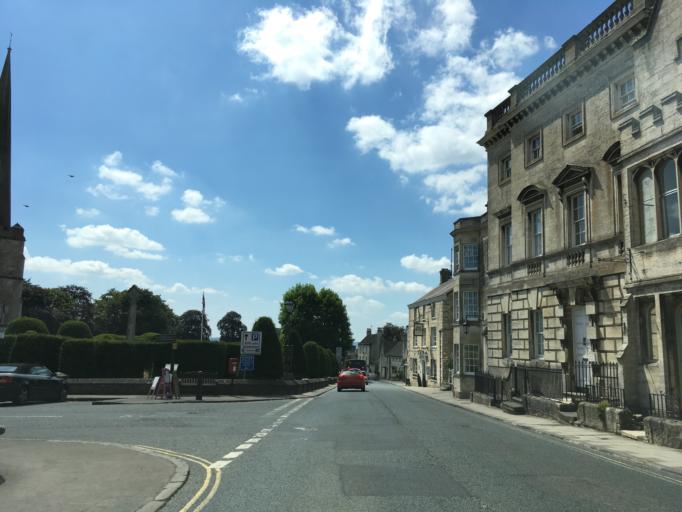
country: GB
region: England
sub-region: Gloucestershire
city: Painswick
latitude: 51.7861
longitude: -2.1949
